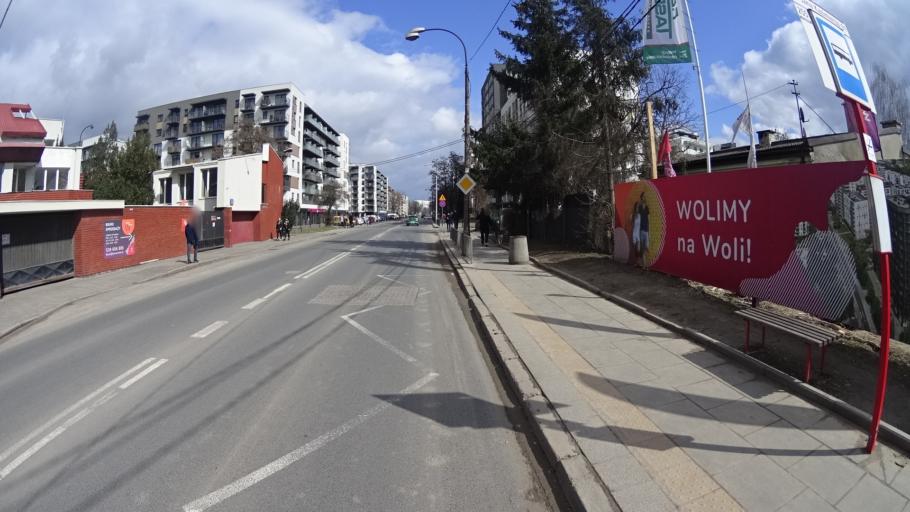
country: PL
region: Masovian Voivodeship
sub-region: Warszawa
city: Bemowo
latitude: 52.2223
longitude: 20.9375
